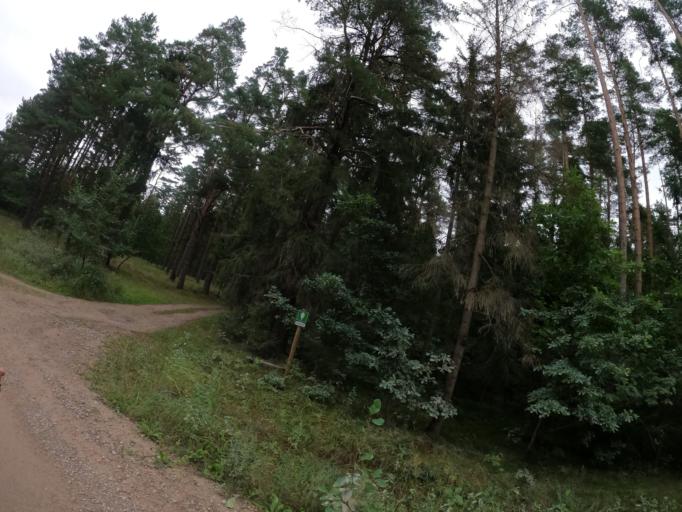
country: LV
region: Kuldigas Rajons
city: Kuldiga
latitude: 57.0022
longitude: 21.9802
